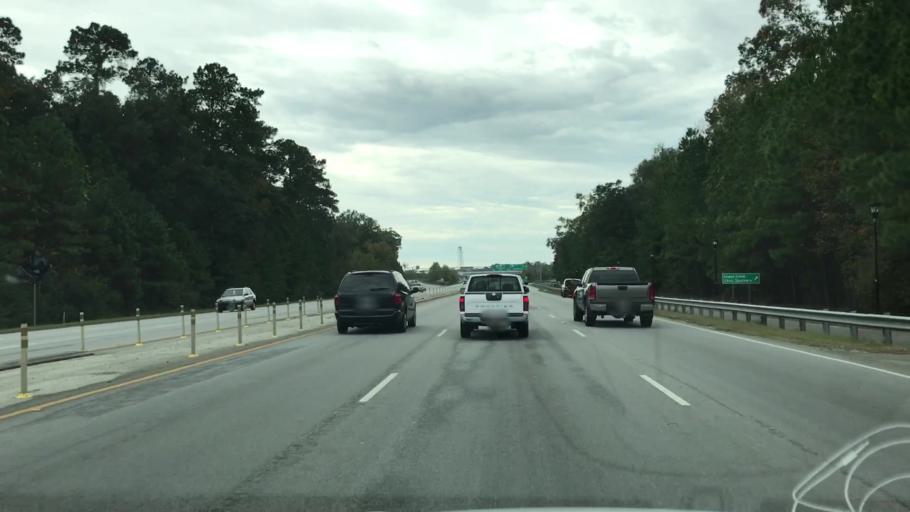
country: US
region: South Carolina
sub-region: Berkeley County
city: Goose Creek
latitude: 32.9811
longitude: -80.0429
